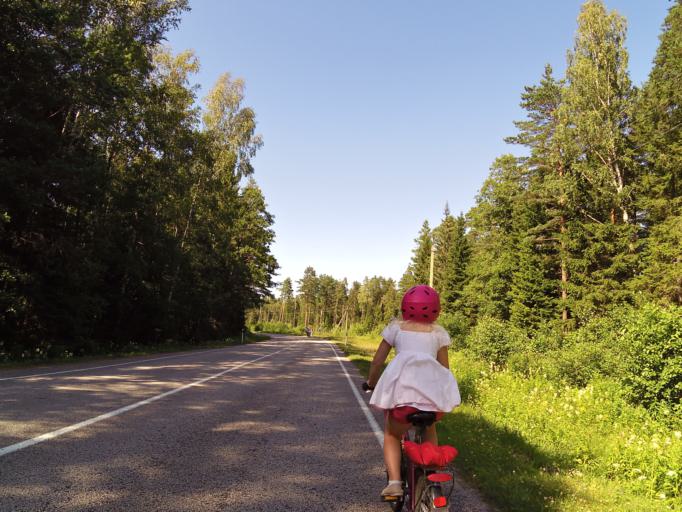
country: EE
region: Hiiumaa
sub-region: Kaerdla linn
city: Kardla
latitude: 58.8610
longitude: 22.4648
